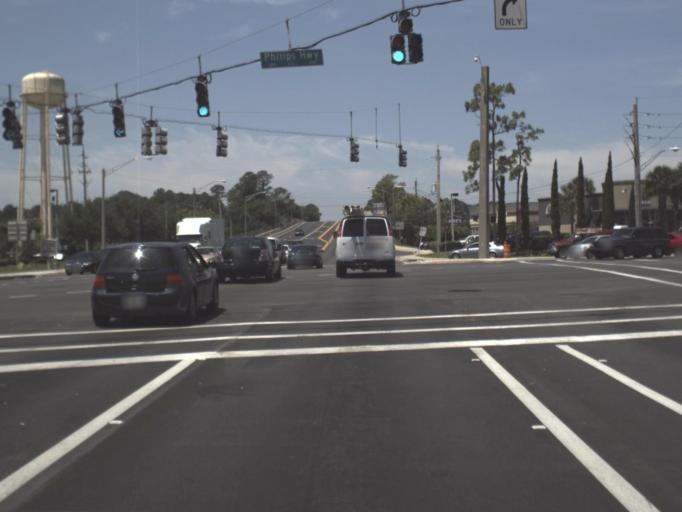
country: US
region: Florida
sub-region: Saint Johns County
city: Fruit Cove
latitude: 30.2208
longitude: -81.5854
